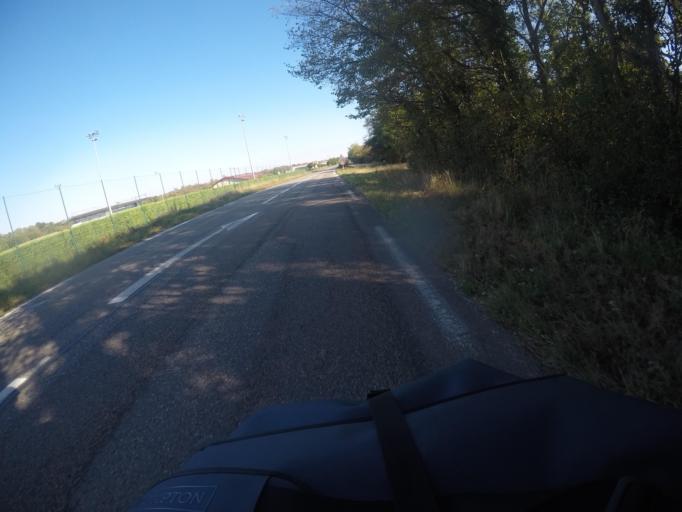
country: FR
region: Alsace
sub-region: Departement du Haut-Rhin
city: Kembs
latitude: 47.6674
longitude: 7.4985
